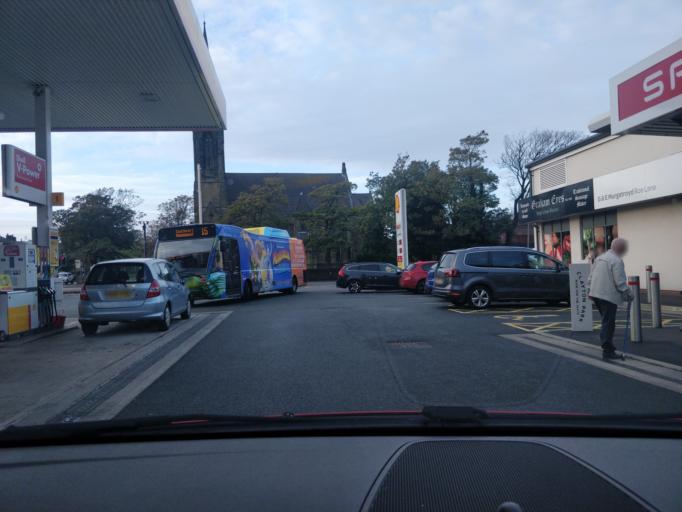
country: GB
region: England
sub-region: Sefton
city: Southport
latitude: 53.6501
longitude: -2.9855
